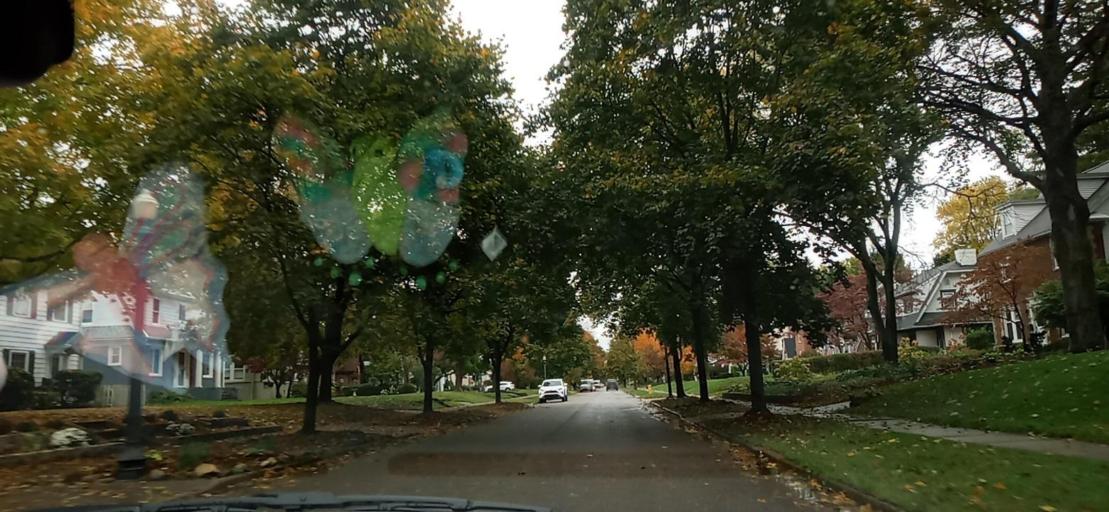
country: US
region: Ohio
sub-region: Summit County
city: Akron
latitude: 41.1071
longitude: -81.5599
